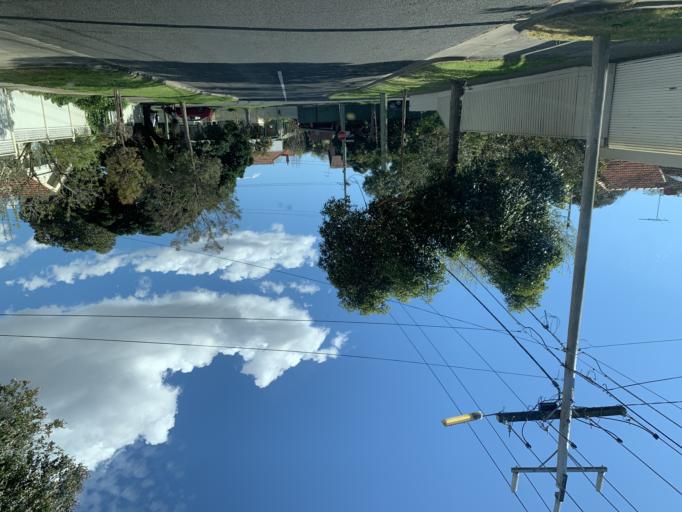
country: AU
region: Victoria
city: Hampton
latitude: -37.9504
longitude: 145.0135
